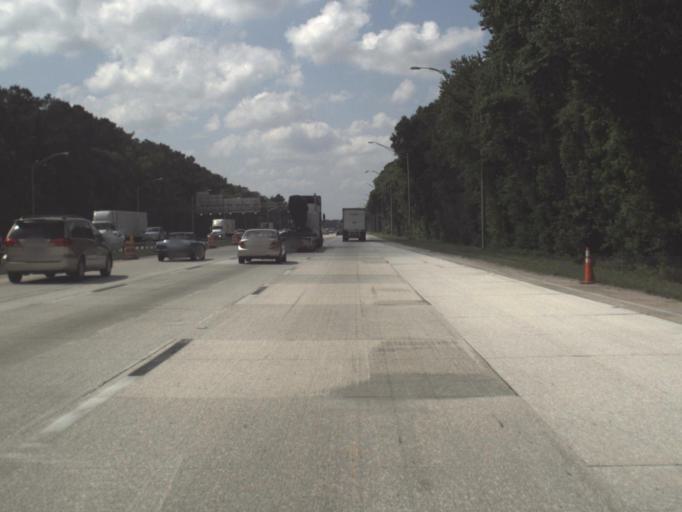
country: US
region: Florida
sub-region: Saint Johns County
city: Fruit Cove
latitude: 30.2249
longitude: -81.5737
